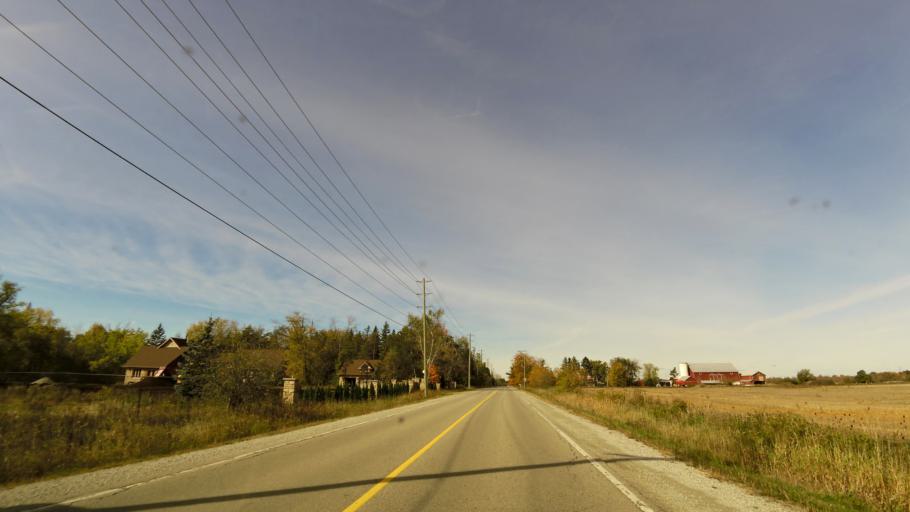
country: CA
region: Ontario
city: Oakville
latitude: 43.5071
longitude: -79.7664
